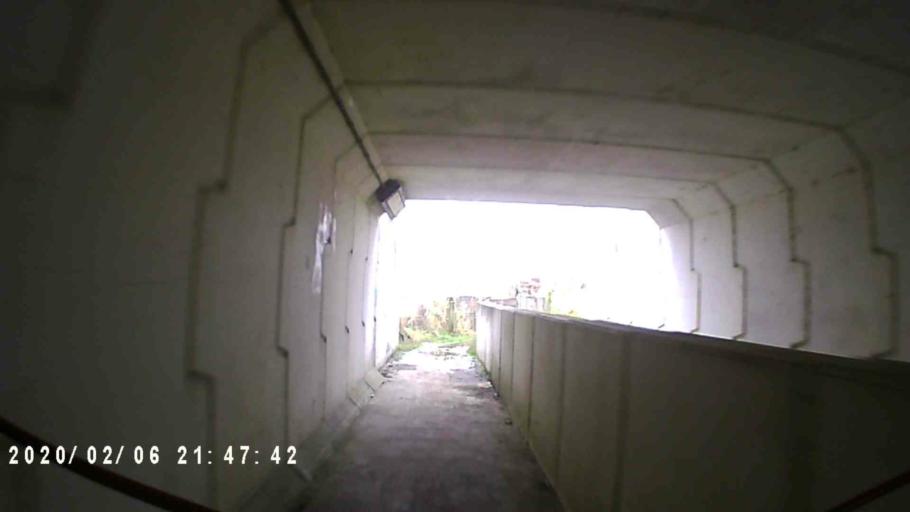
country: NL
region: Groningen
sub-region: Gemeente Zuidhorn
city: Noordhorn
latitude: 53.2553
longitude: 6.3791
